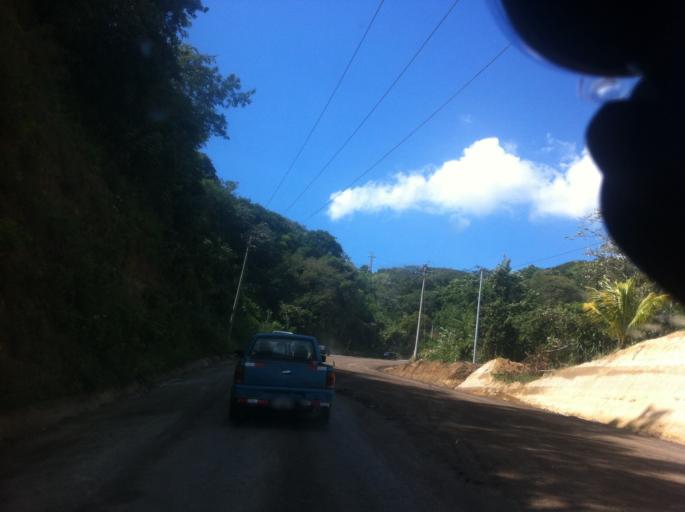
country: NI
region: Managua
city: Ciudad Sandino
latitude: 12.0802
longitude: -86.3762
